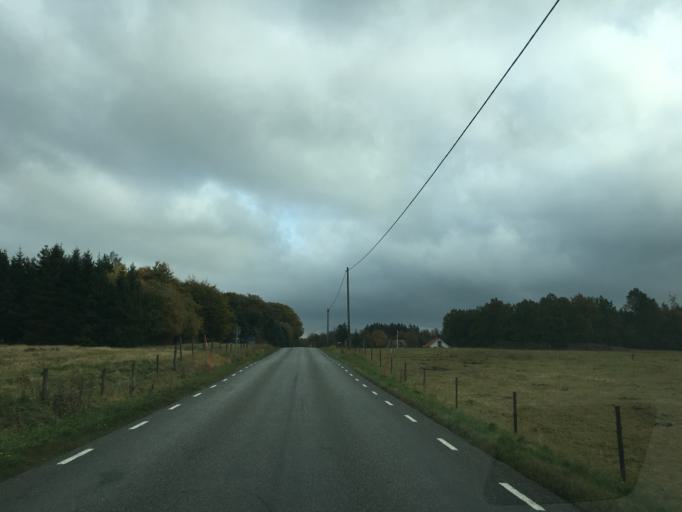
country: SE
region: Skane
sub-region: Tomelilla Kommun
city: Tomelilla
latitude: 55.6380
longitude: 14.0726
